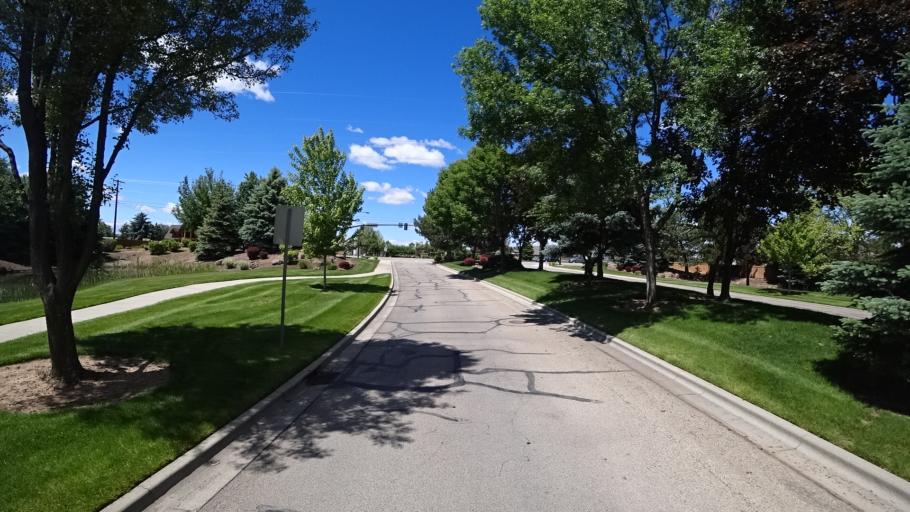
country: US
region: Idaho
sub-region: Ada County
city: Meridian
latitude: 43.6415
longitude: -116.3533
